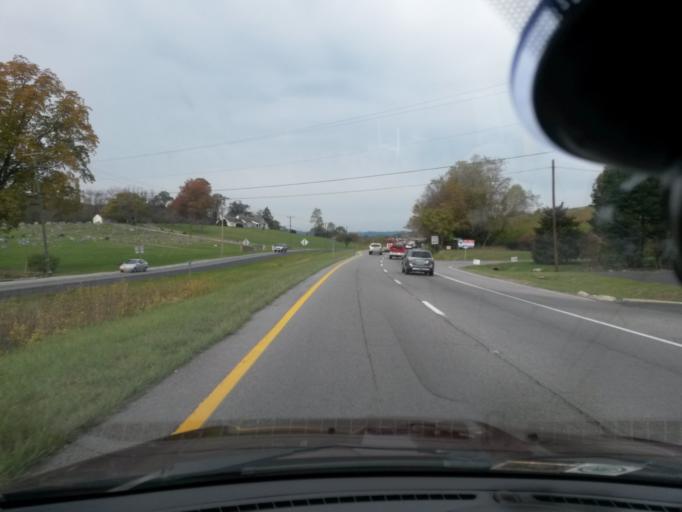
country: US
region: Virginia
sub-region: Botetourt County
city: Daleville
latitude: 37.3978
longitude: -79.9092
